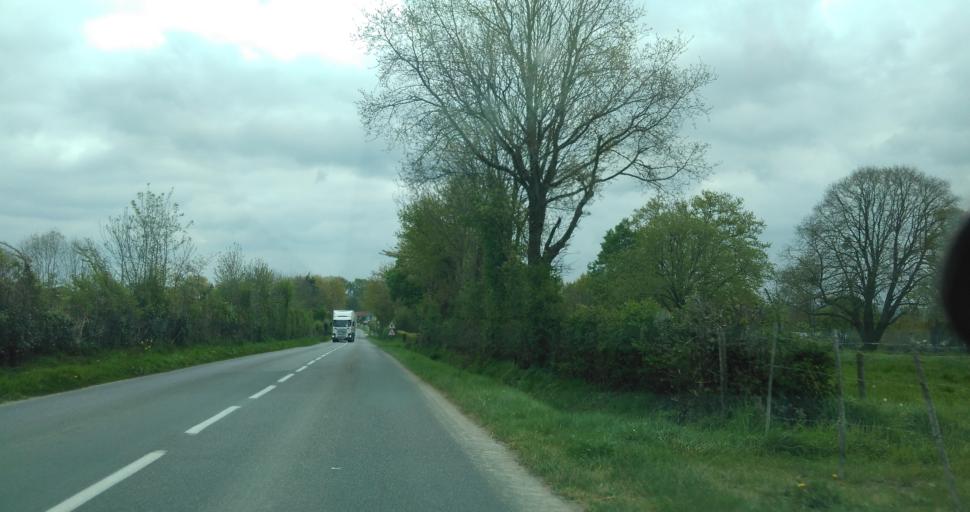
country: FR
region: Poitou-Charentes
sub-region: Departement des Deux-Sevres
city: Moncoutant
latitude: 46.7213
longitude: -0.5592
